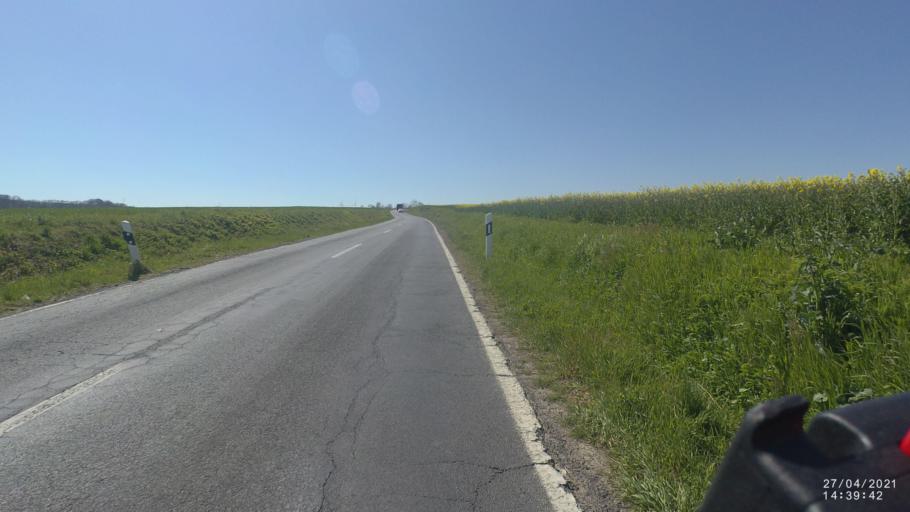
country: DE
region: Rheinland-Pfalz
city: Kollig
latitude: 50.2698
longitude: 7.2918
